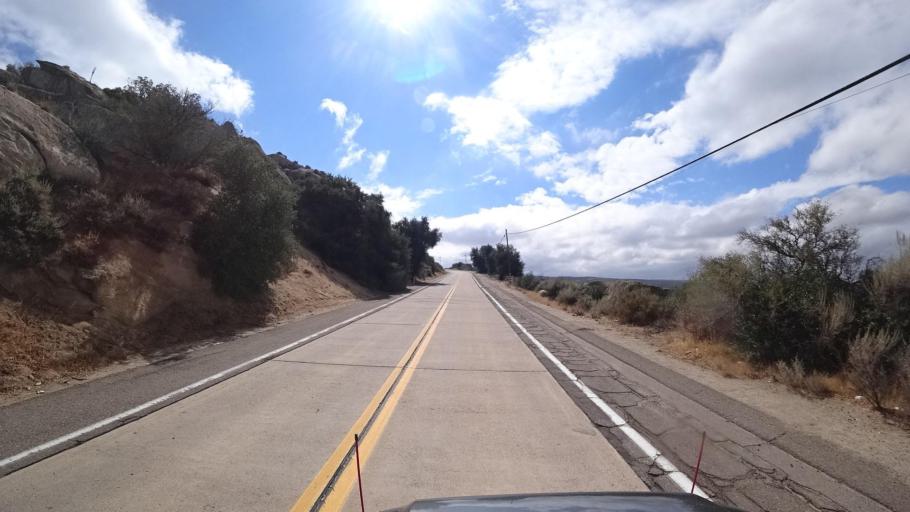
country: US
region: California
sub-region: San Diego County
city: Campo
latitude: 32.6788
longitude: -116.3327
